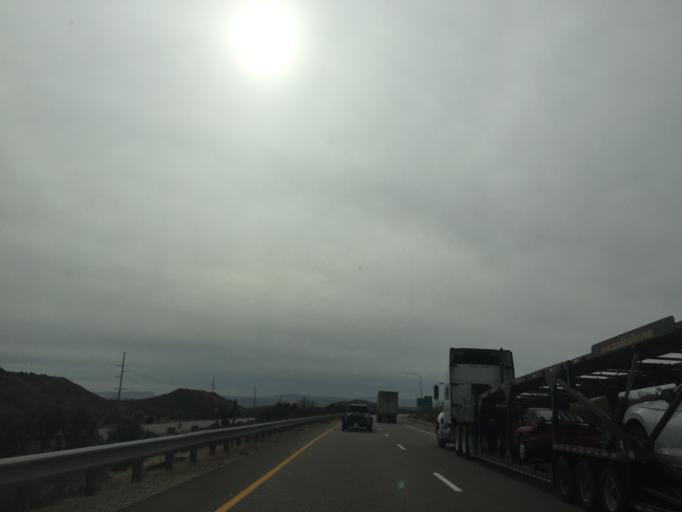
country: US
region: Utah
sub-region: Washington County
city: Toquerville
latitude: 37.2896
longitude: -113.3022
